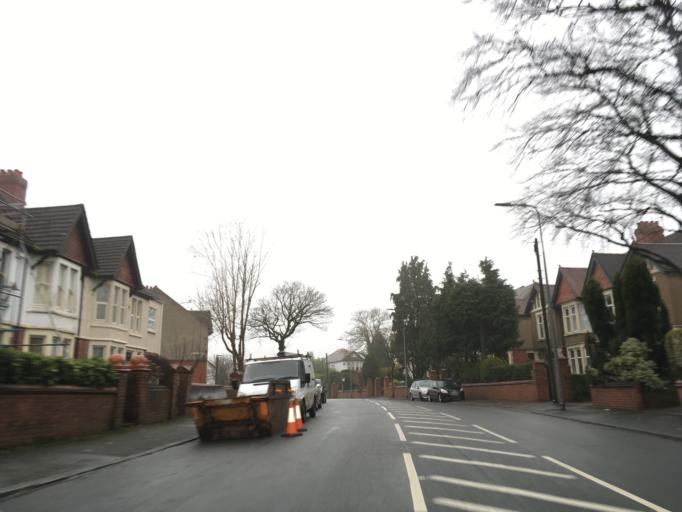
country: GB
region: Wales
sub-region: Cardiff
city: Cardiff
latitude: 51.5040
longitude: -3.1584
